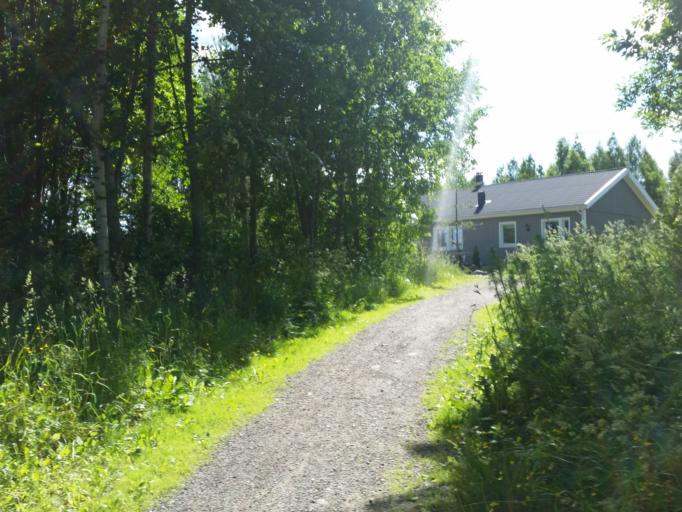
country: FI
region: Northern Savo
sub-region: Varkaus
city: Varkaus
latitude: 62.3372
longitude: 27.9035
